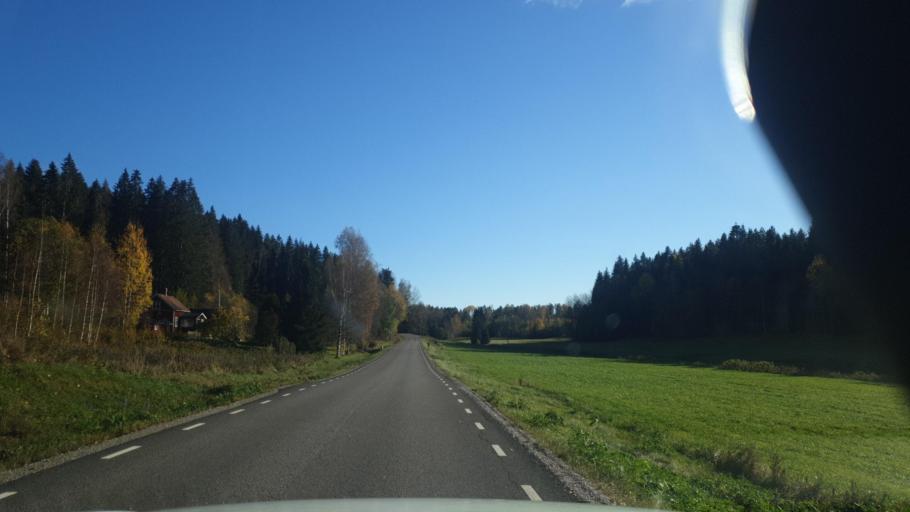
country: SE
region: Vaermland
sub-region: Arvika Kommun
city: Arvika
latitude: 59.6442
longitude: 12.8086
